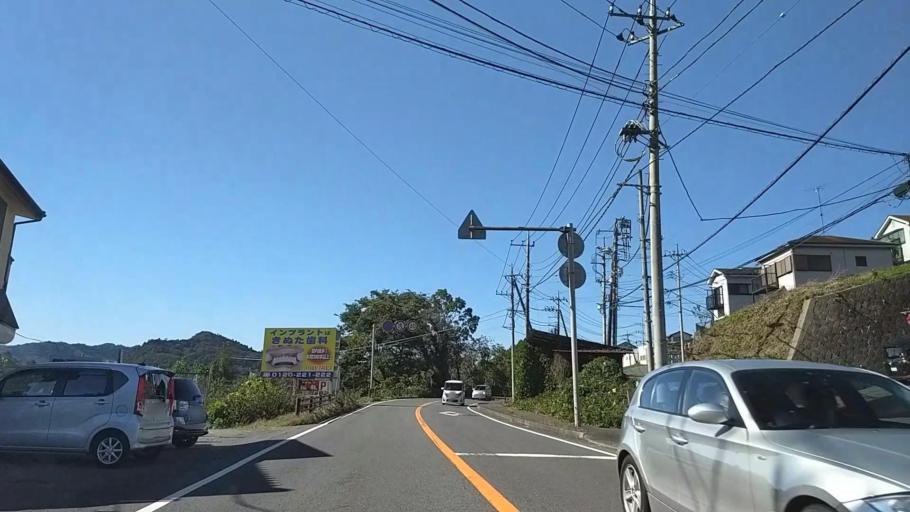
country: JP
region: Yamanashi
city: Uenohara
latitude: 35.6129
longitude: 139.1633
